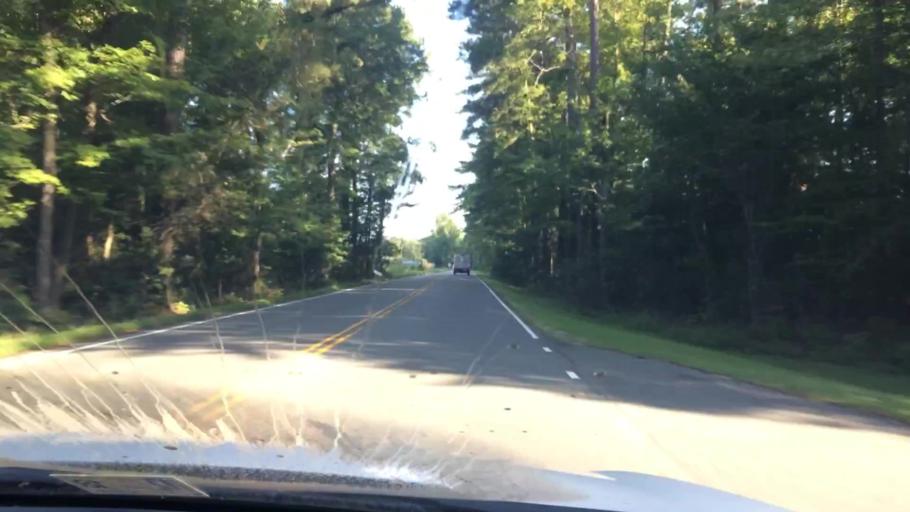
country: US
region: Virginia
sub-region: King William County
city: West Point
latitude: 37.4445
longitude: -76.8383
